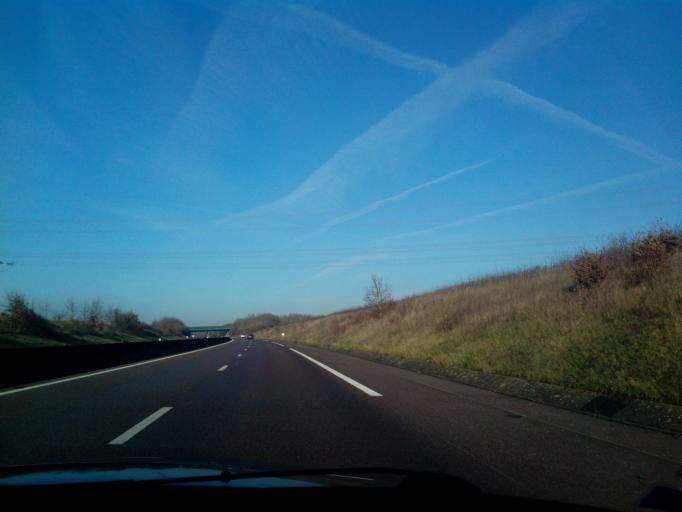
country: FR
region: Picardie
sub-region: Departement de l'Oise
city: Saint-Crepin-Ibouvillers
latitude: 49.2675
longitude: 2.0924
